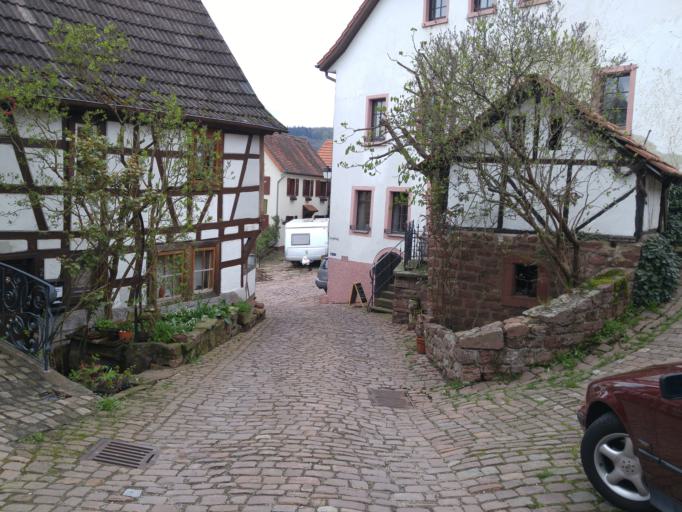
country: DE
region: Hesse
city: Neckarsteinach
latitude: 49.3988
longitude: 8.8364
